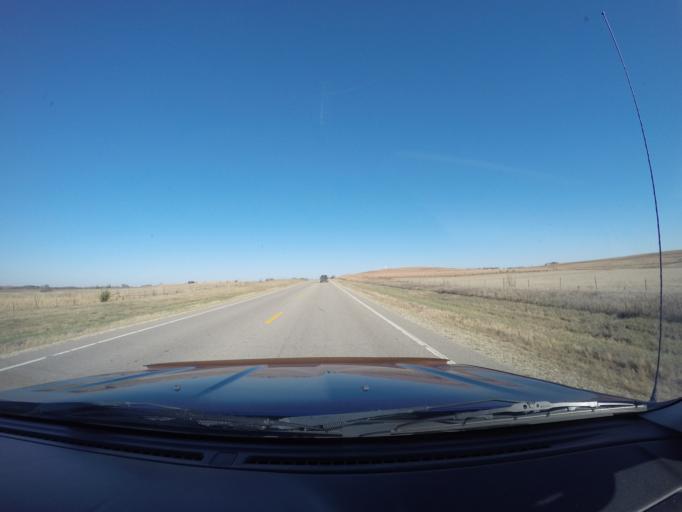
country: US
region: Kansas
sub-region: Riley County
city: Ogden
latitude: 39.3361
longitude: -96.7562
